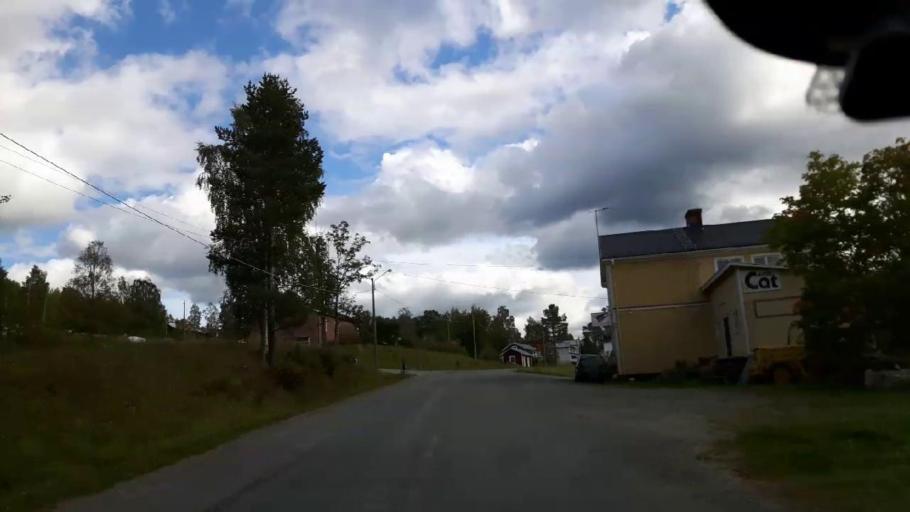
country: SE
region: Jaemtland
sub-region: Stroemsunds Kommun
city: Stroemsund
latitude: 63.4245
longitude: 15.8218
